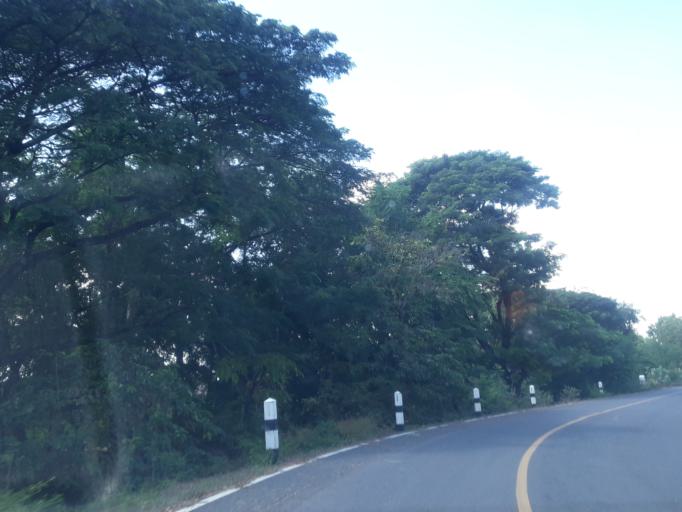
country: TH
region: Lop Buri
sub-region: Amphoe Tha Luang
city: Tha Luang
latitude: 15.0522
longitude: 101.0249
